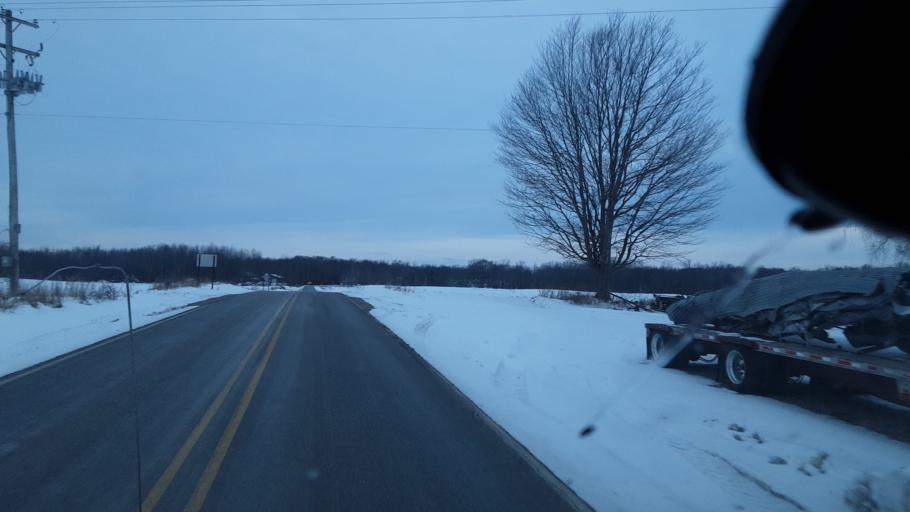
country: US
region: Michigan
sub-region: Ingham County
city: Leslie
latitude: 42.4429
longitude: -84.3150
